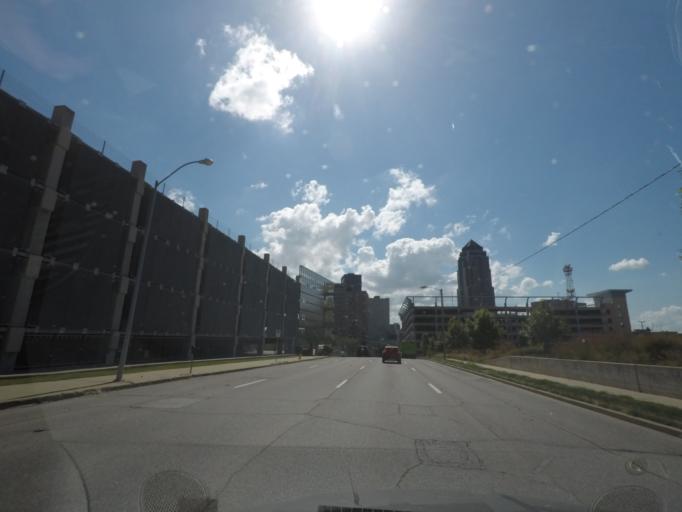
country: US
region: Iowa
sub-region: Polk County
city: Des Moines
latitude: 41.5928
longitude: -93.6269
